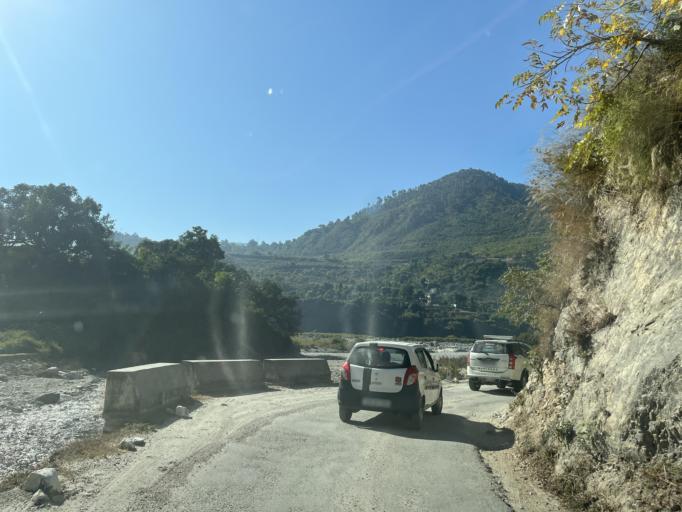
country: IN
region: Uttarakhand
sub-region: Naini Tal
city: Naini Tal
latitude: 29.5126
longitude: 79.4766
